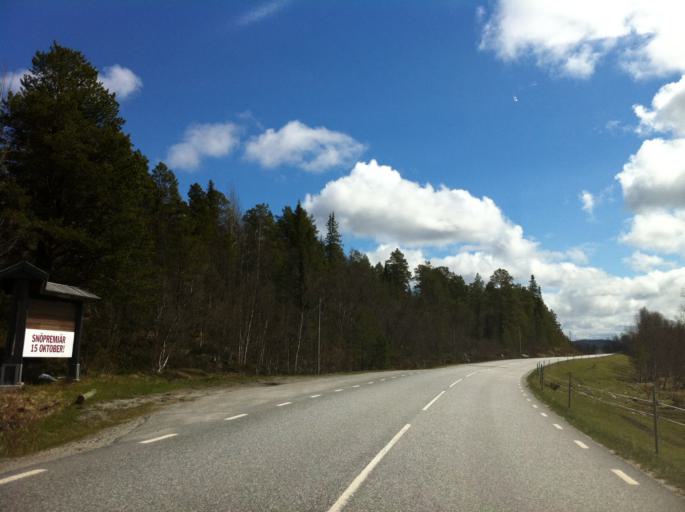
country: NO
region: Sor-Trondelag
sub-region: Tydal
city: Aas
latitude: 62.6193
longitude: 12.4764
